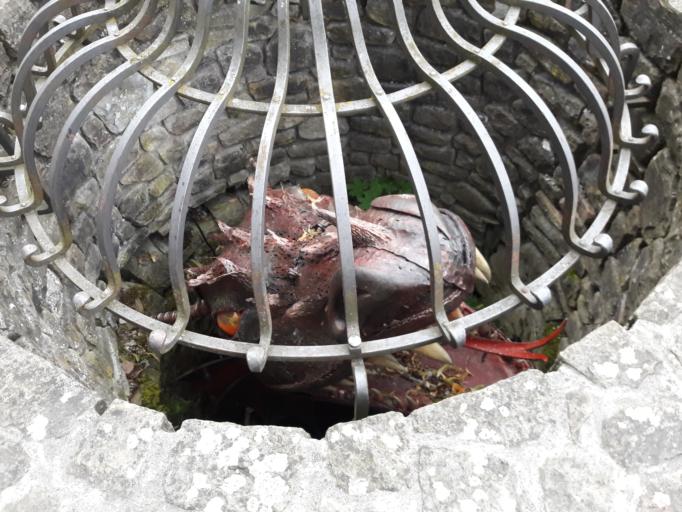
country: SK
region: Zilinsky
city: Bytca
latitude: 49.2208
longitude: 18.5590
